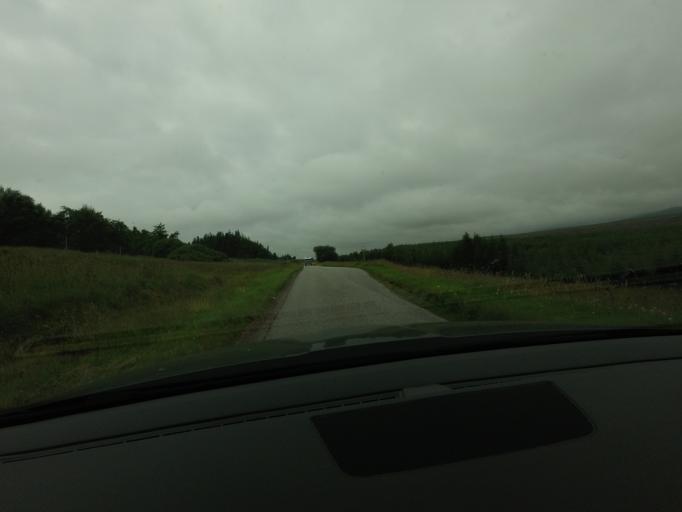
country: GB
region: Scotland
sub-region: Highland
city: Alness
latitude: 58.1286
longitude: -4.4575
